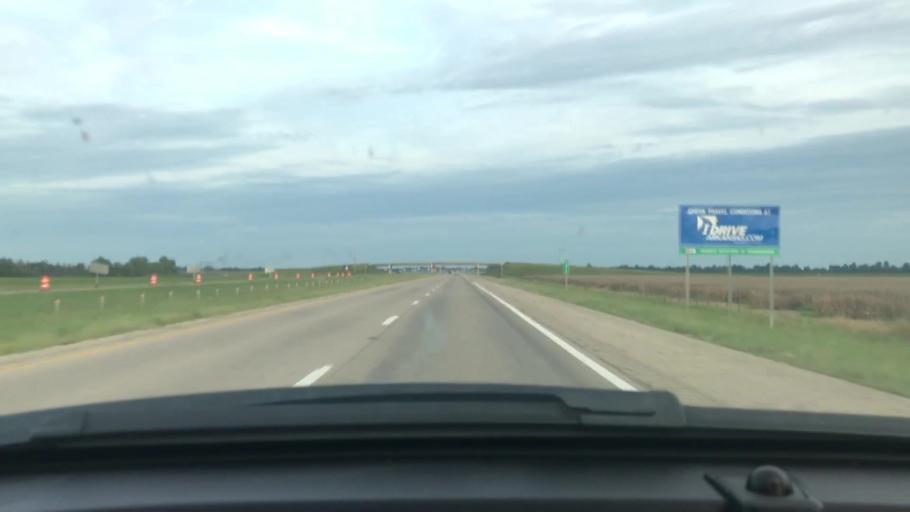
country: US
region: Arkansas
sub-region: Craighead County
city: Bay
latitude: 35.7087
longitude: -90.5706
